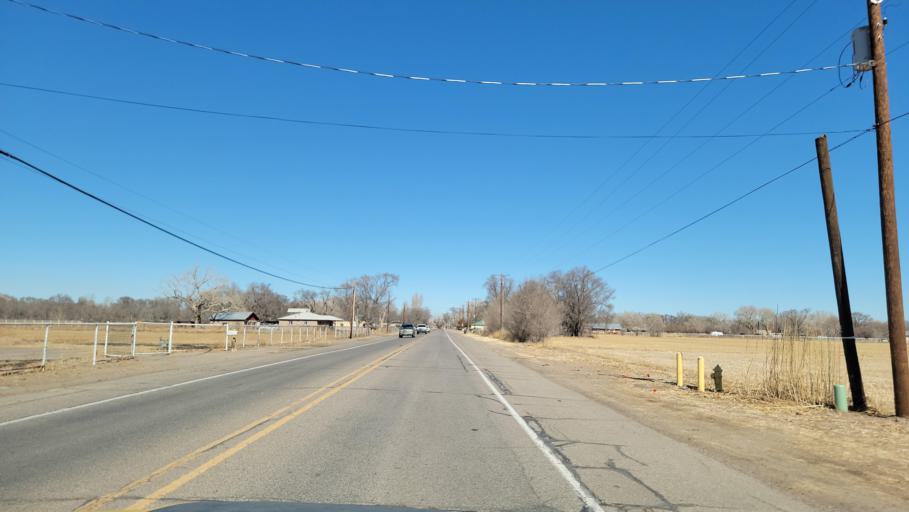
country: US
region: New Mexico
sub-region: Bernalillo County
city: South Valley
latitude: 34.9671
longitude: -106.6956
